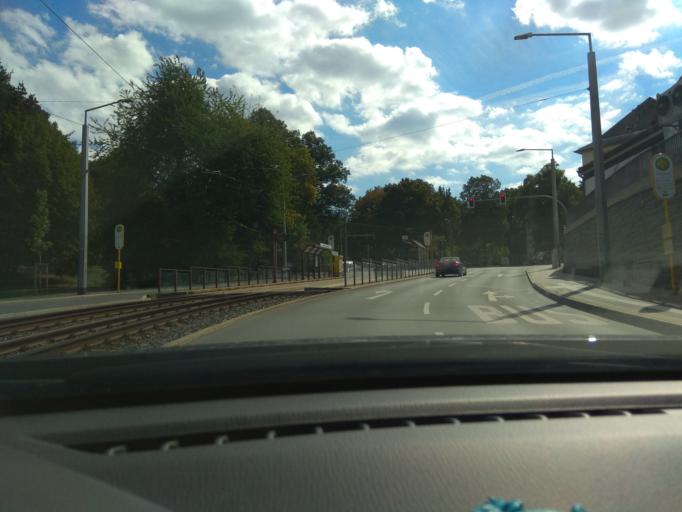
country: DE
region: Saxony
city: Plauen
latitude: 50.4926
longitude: 12.1495
